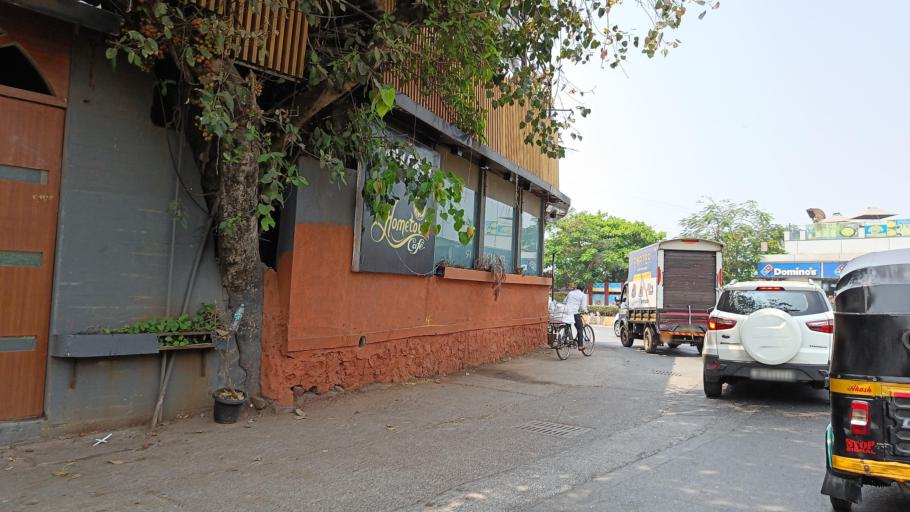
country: IN
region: Maharashtra
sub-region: Mumbai Suburban
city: Mumbai
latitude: 19.0982
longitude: 72.8270
